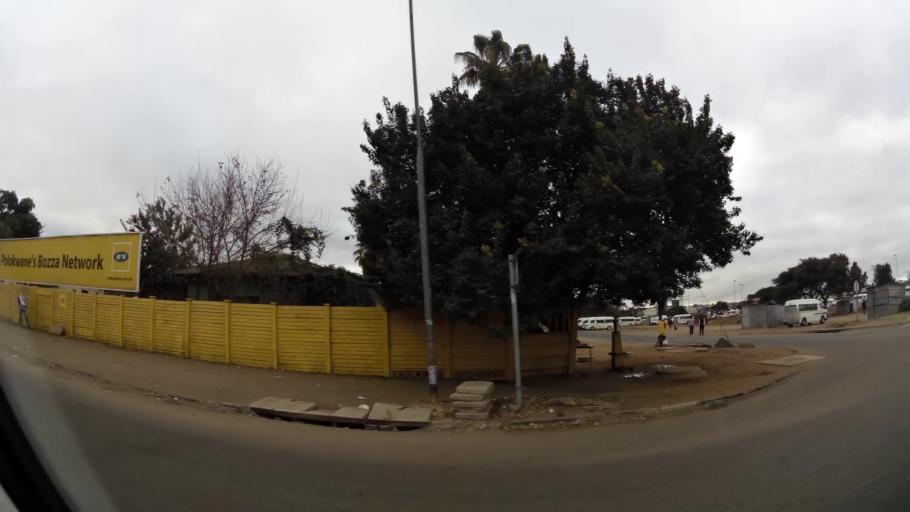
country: ZA
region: Limpopo
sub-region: Capricorn District Municipality
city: Polokwane
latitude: -23.9043
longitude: 29.4426
